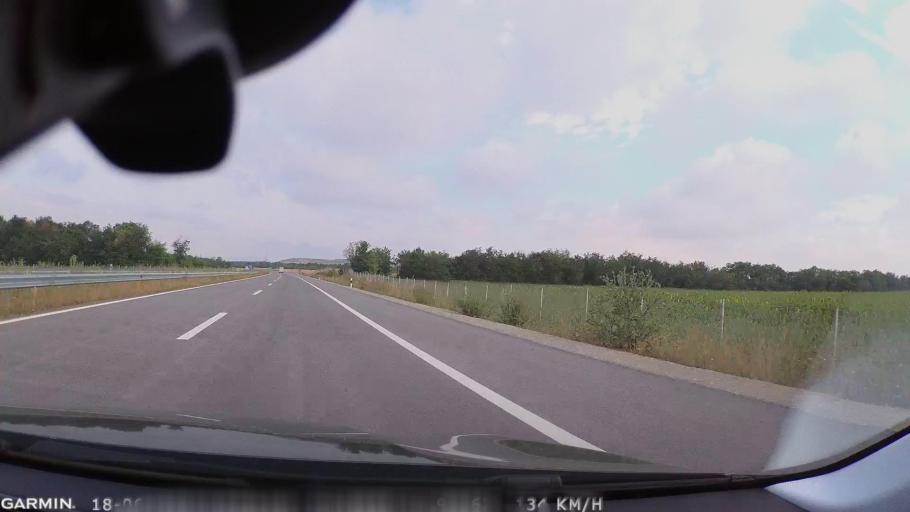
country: MK
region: Sveti Nikole
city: Sveti Nikole
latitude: 41.8393
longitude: 21.9834
